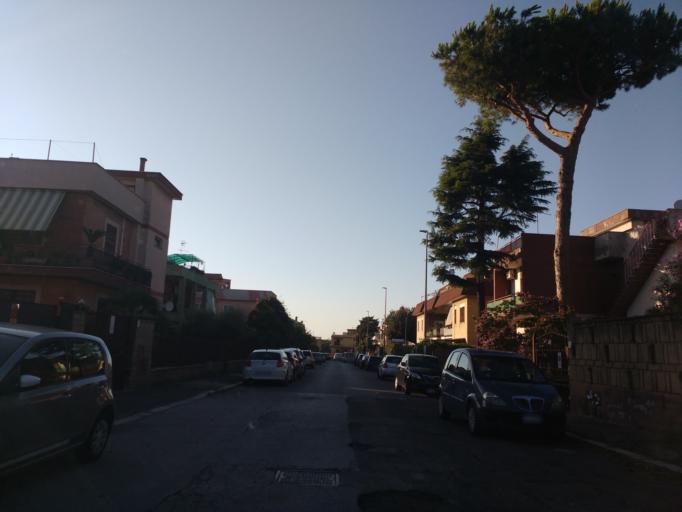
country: IT
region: Latium
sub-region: Citta metropolitana di Roma Capitale
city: Vitinia
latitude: 41.7829
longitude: 12.3695
